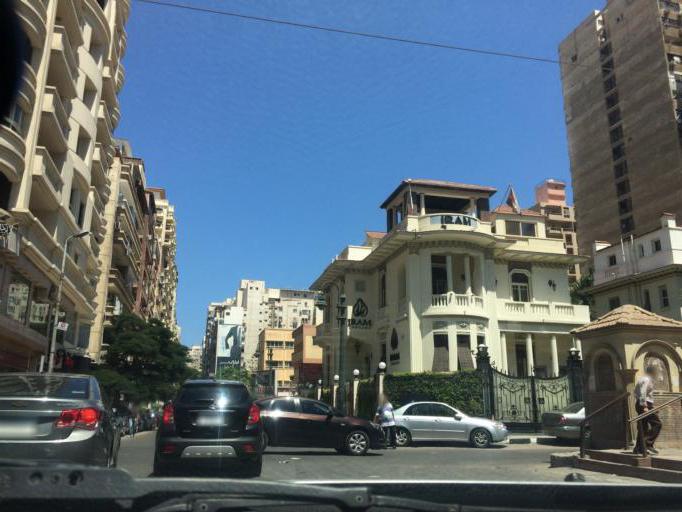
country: EG
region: Alexandria
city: Alexandria
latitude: 31.2287
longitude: 29.9513
